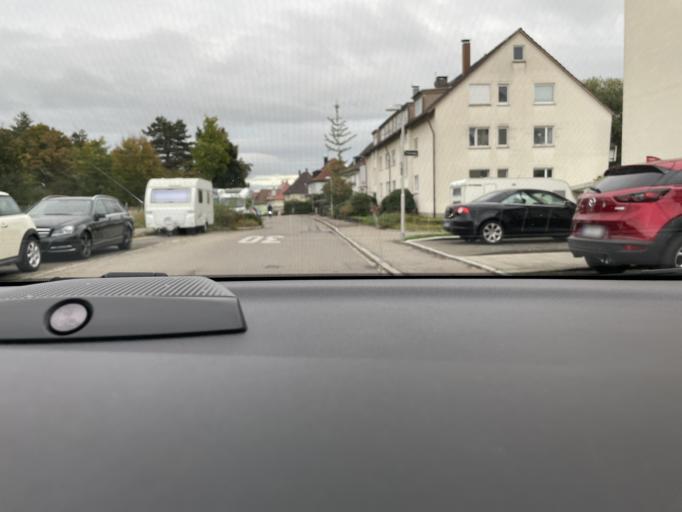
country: DE
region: Baden-Wuerttemberg
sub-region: Tuebingen Region
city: Friedrichshafen
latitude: 47.6584
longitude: 9.4586
